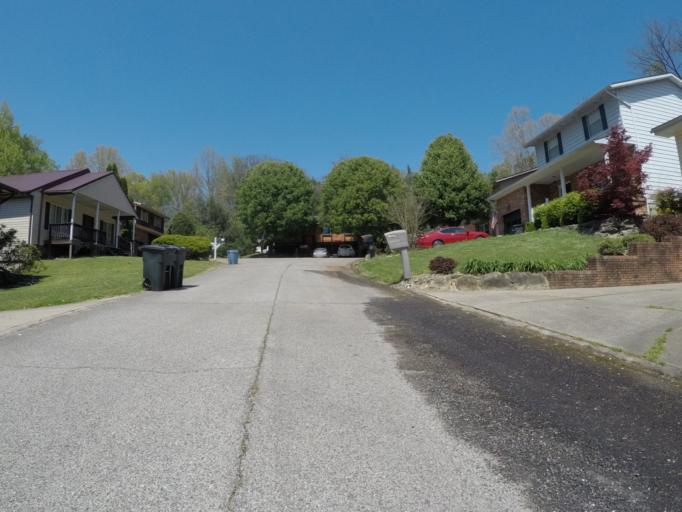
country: US
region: West Virginia
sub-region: Cabell County
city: Pea Ridge
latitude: 38.4080
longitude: -82.3427
